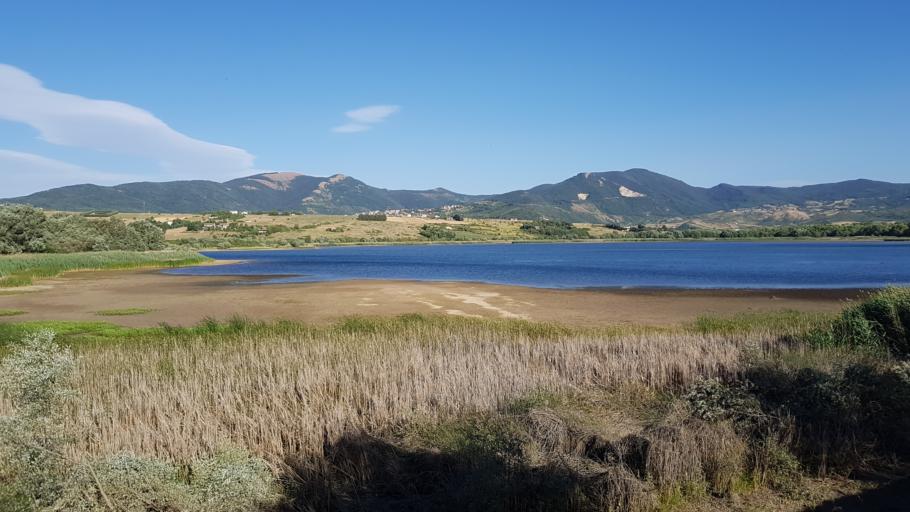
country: IT
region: Basilicate
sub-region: Provincia di Potenza
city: Pignola
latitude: 40.5934
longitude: 15.7428
